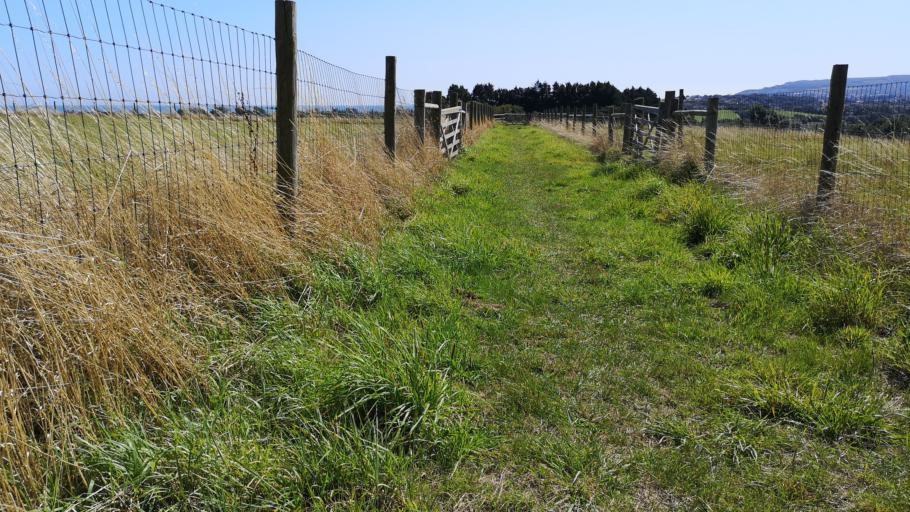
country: GB
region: England
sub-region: Isle of Wight
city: Brading
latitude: 50.6742
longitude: -1.1555
